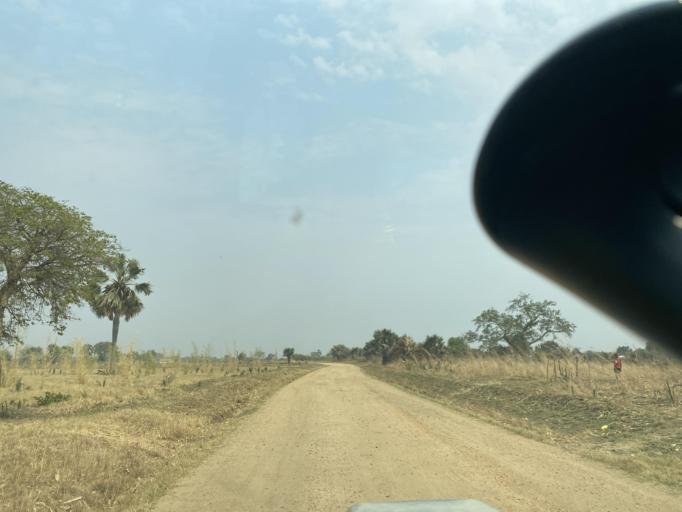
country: ZM
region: Lusaka
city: Kafue
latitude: -15.6495
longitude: 28.0478
